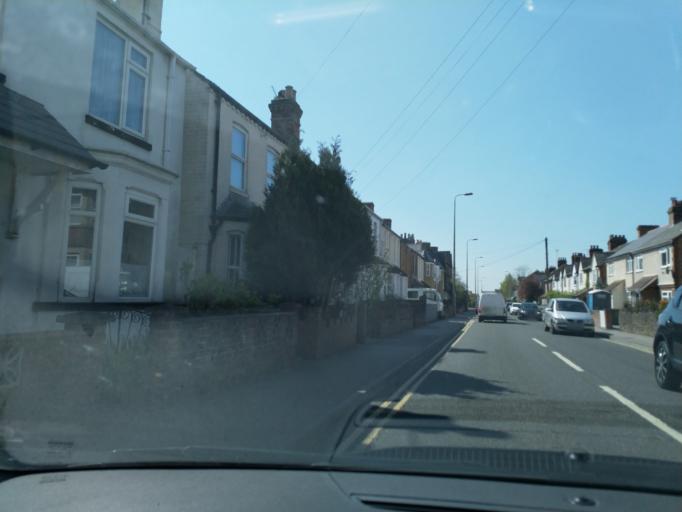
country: GB
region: England
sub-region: Oxfordshire
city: Cowley
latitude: 51.7390
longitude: -1.2065
